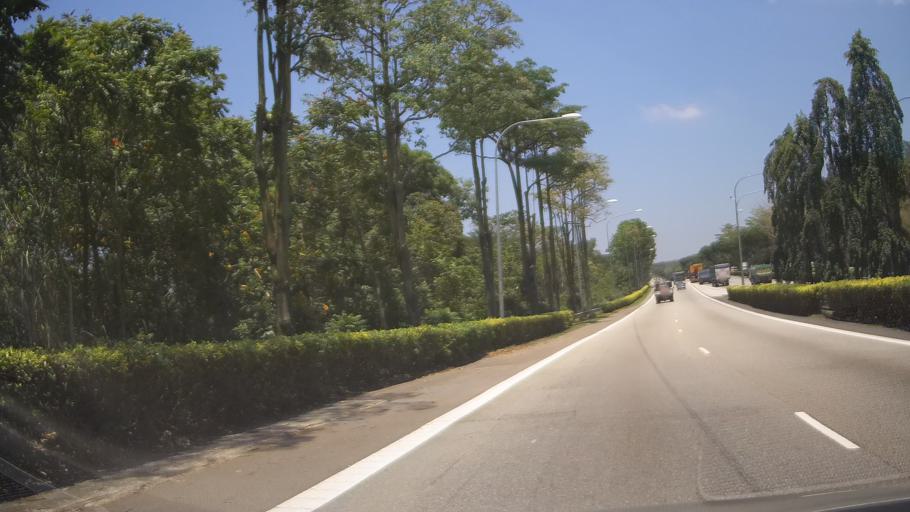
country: MY
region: Johor
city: Johor Bahru
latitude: 1.3672
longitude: 103.7102
